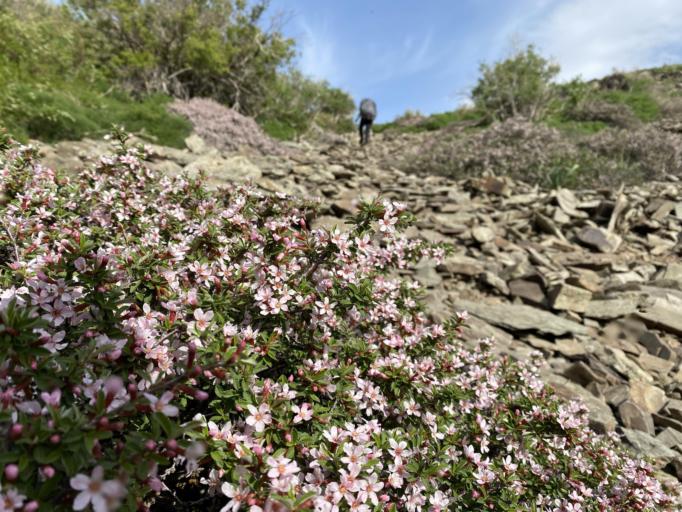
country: KZ
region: Ongtustik Qazaqstan
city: Kentau
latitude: 43.8432
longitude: 68.5031
